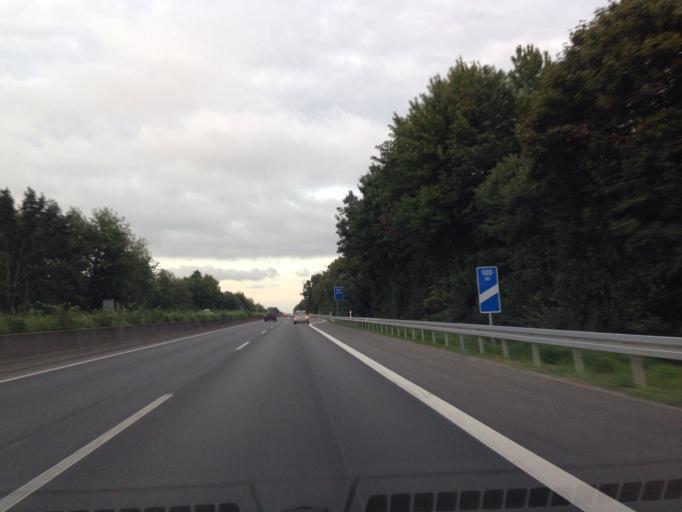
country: DE
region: North Rhine-Westphalia
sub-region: Regierungsbezirk Dusseldorf
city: Neubrueck
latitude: 51.1379
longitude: 6.6146
